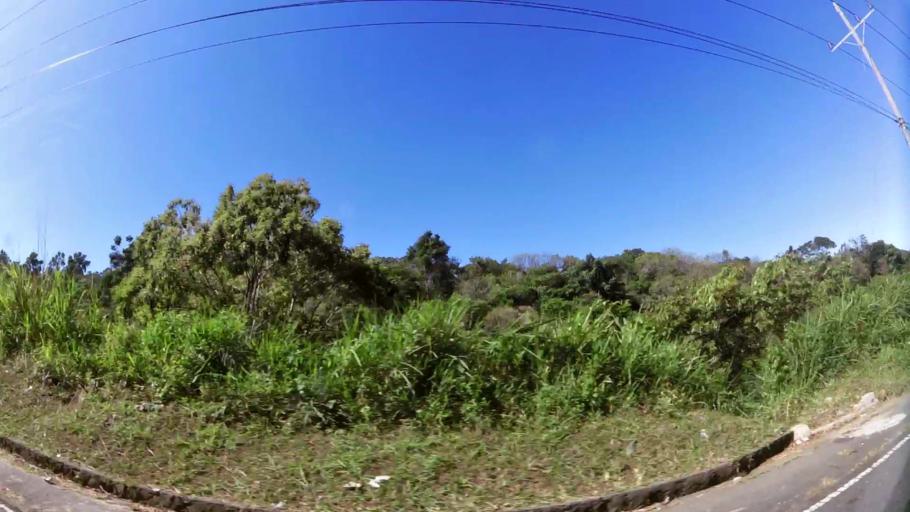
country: SV
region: Ahuachapan
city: Ahuachapan
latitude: 13.9012
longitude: -89.8329
